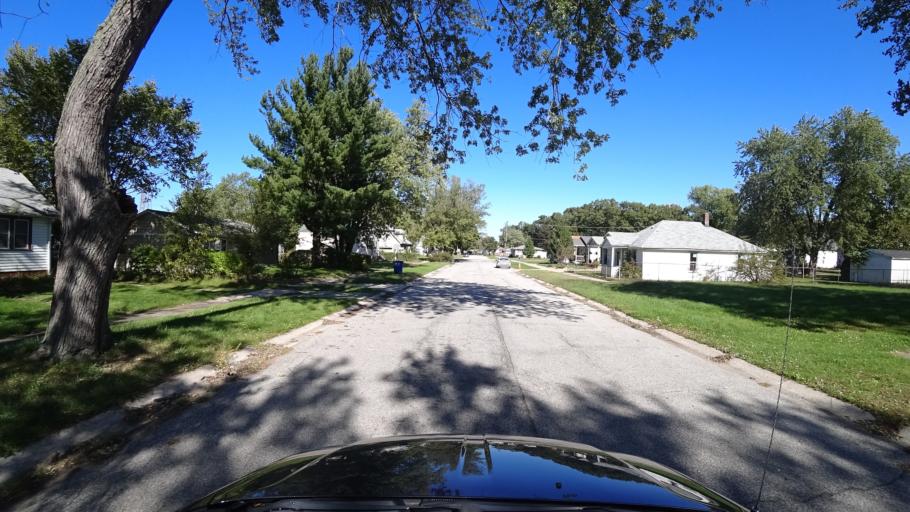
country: US
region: Indiana
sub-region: LaPorte County
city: Michigan City
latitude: 41.7080
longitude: -86.9194
